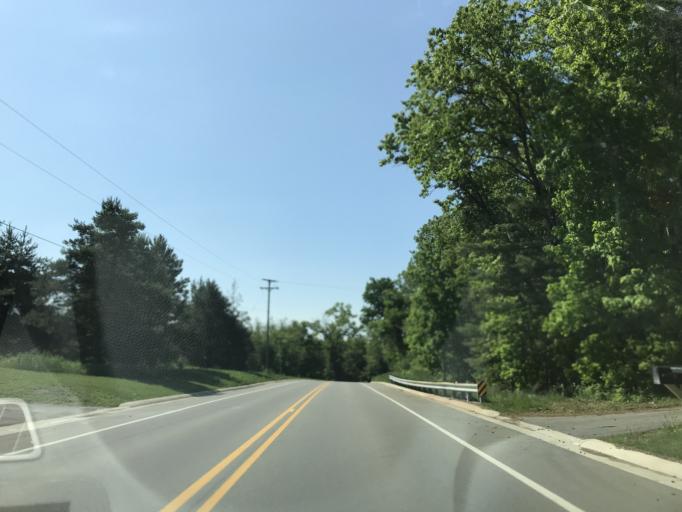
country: US
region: Michigan
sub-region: Oakland County
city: South Lyon
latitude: 42.4749
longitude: -83.6965
